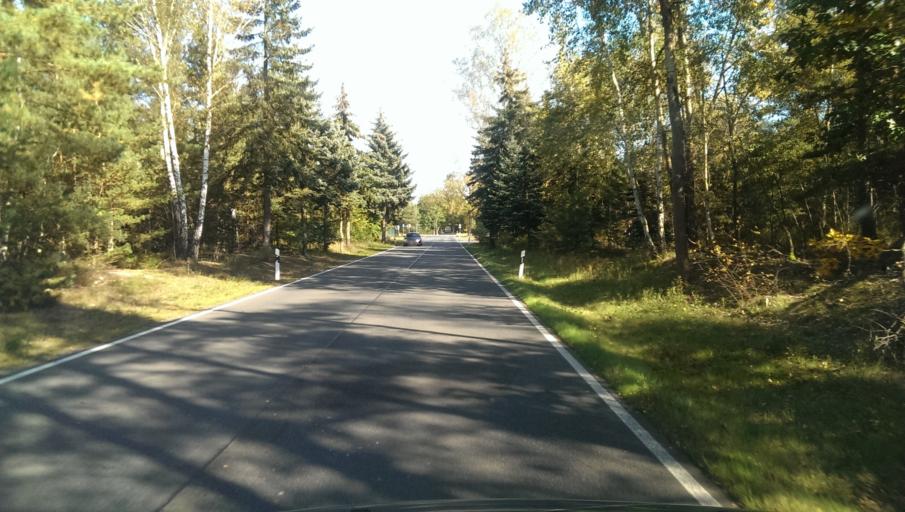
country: DE
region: Brandenburg
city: Halbe
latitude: 52.0279
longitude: 13.7291
